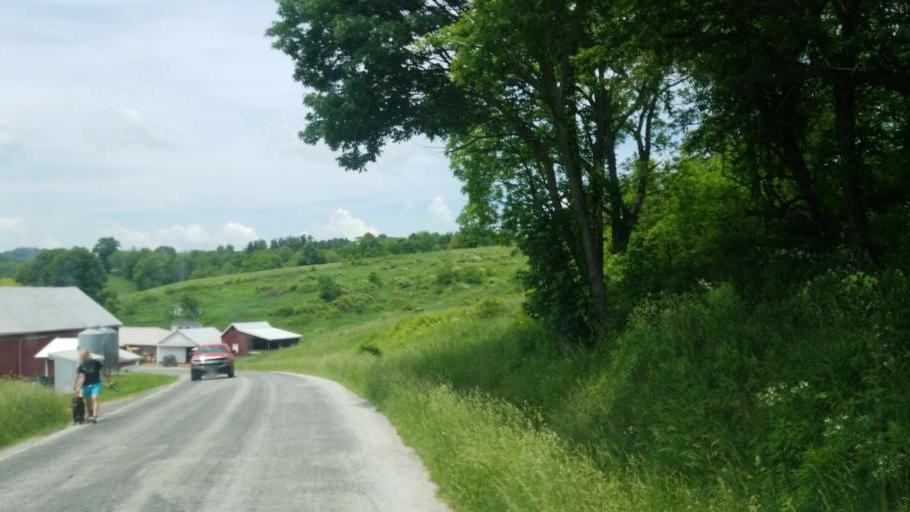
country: US
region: Ohio
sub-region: Coshocton County
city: West Lafayette
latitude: 40.3780
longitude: -81.7594
